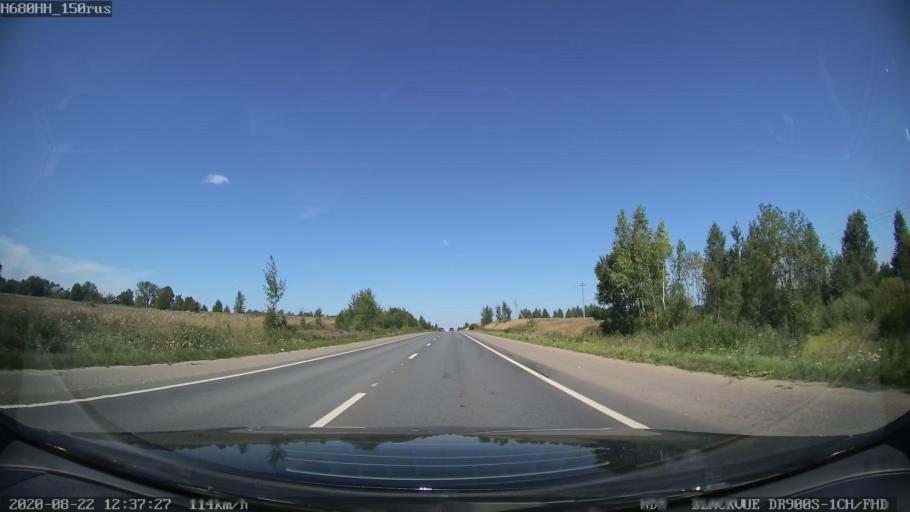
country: RU
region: Tverskaya
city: Rameshki
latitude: 57.2962
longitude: 36.0891
